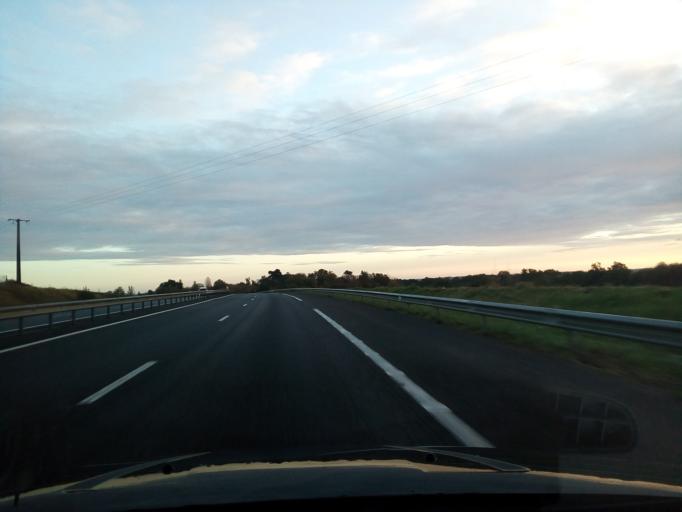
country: FR
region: Poitou-Charentes
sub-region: Departement de la Charente-Maritime
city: Montlieu-la-Garde
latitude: 45.2607
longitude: -0.2520
